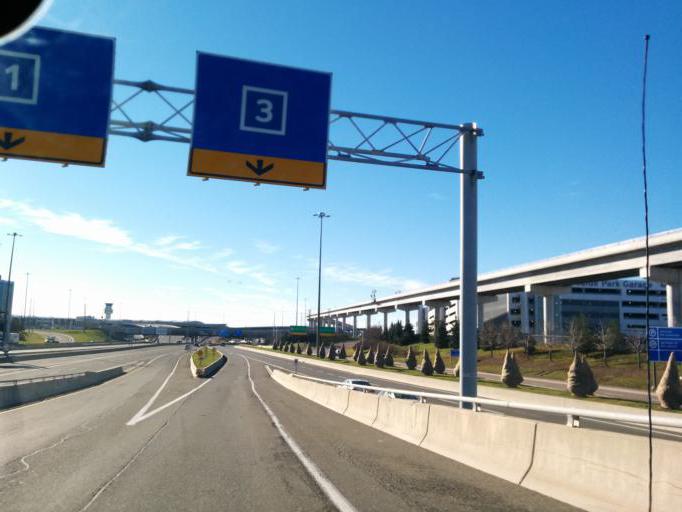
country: CA
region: Ontario
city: Etobicoke
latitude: 43.6929
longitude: -79.6117
